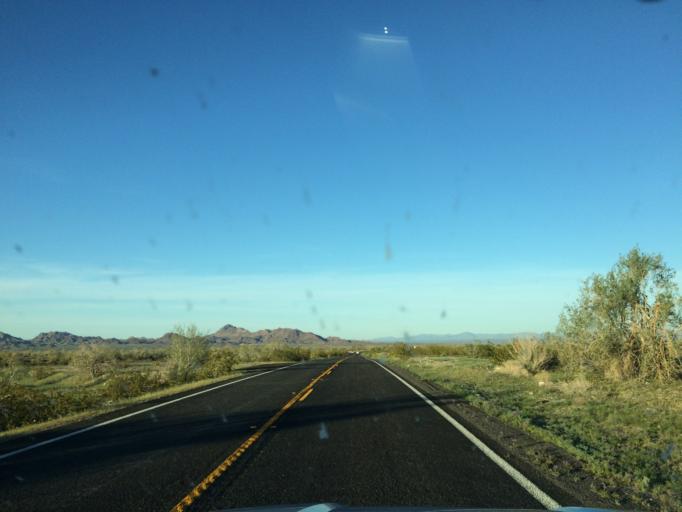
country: US
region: California
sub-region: Riverside County
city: Mesa Verde
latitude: 33.2395
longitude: -114.8338
